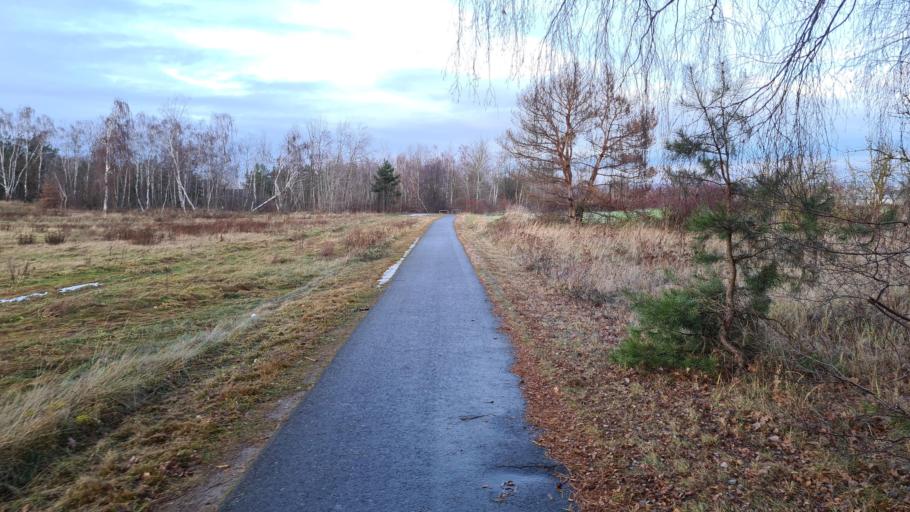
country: DE
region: Brandenburg
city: Groden
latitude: 51.3978
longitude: 13.5827
